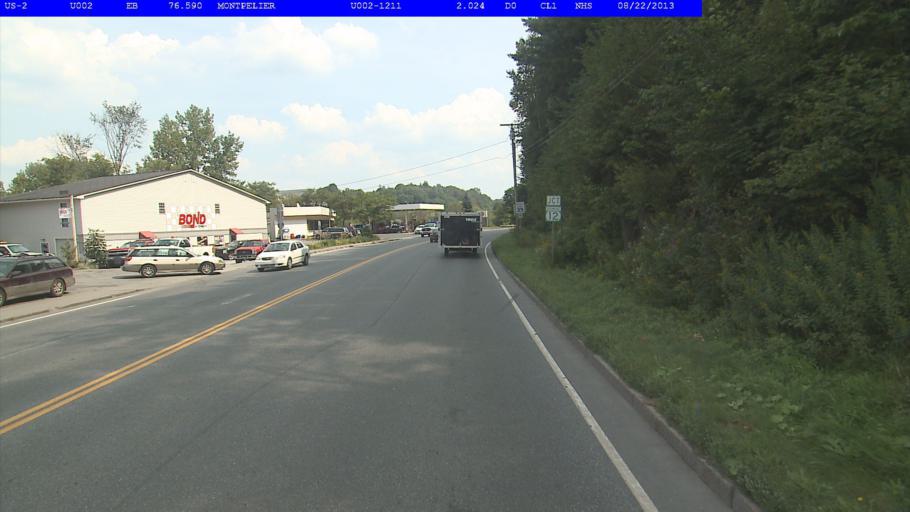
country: US
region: Vermont
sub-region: Washington County
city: Montpelier
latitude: 44.2590
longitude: -72.5799
